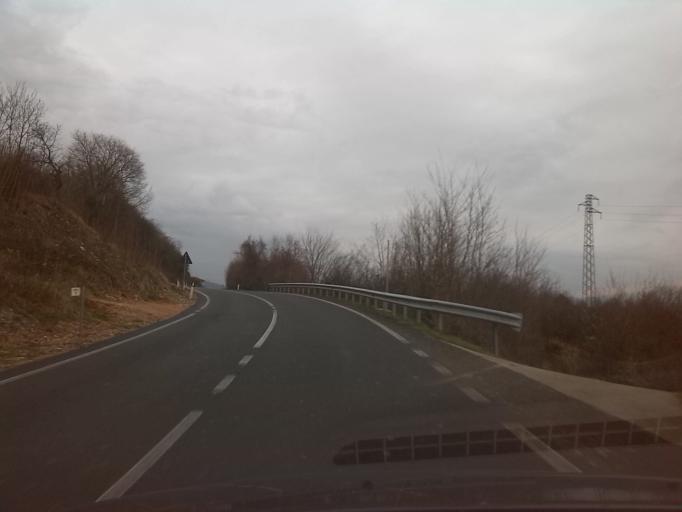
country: IT
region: Friuli Venezia Giulia
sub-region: Provincia di Gorizia
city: Medea
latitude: 45.9222
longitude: 13.4396
